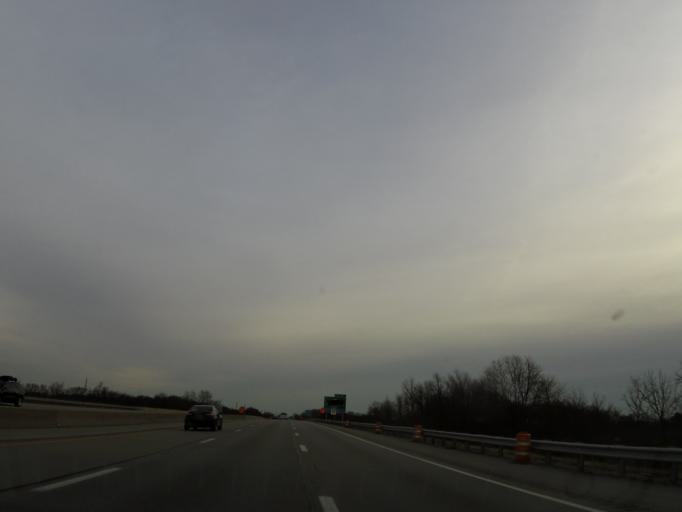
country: US
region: Kentucky
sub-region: Scott County
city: Georgetown
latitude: 38.2663
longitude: -84.5541
